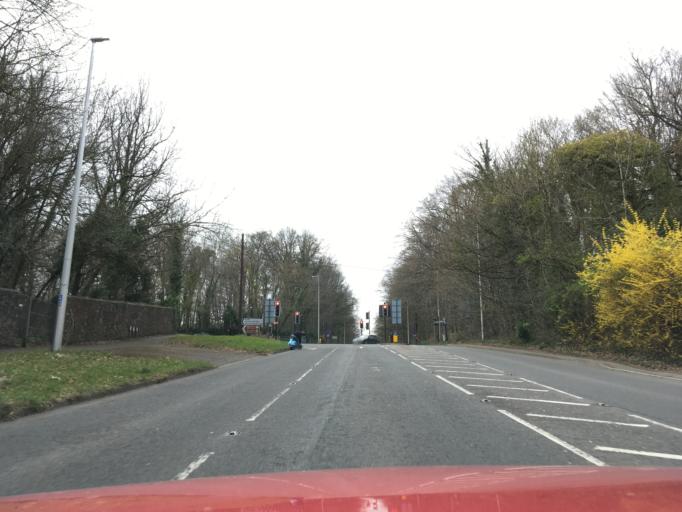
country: GB
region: England
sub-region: North Somerset
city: Long Ashton
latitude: 51.4548
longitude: -2.6449
